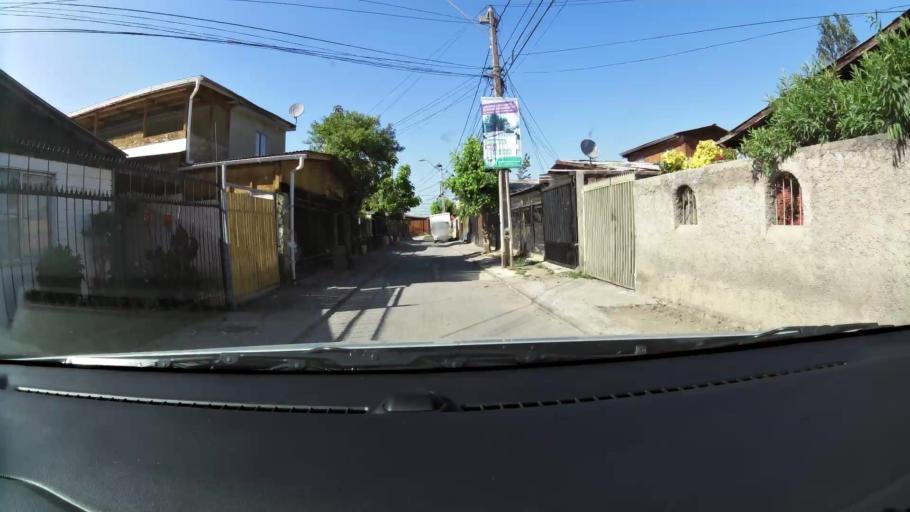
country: CL
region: Santiago Metropolitan
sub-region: Provincia de Maipo
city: San Bernardo
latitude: -33.5687
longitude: -70.6983
